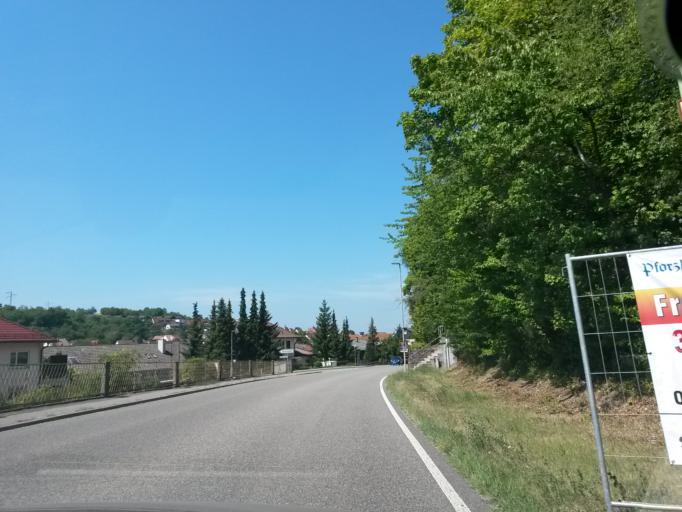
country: DE
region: Baden-Wuerttemberg
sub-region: Karlsruhe Region
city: Birkenfeld
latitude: 48.8924
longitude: 8.6086
